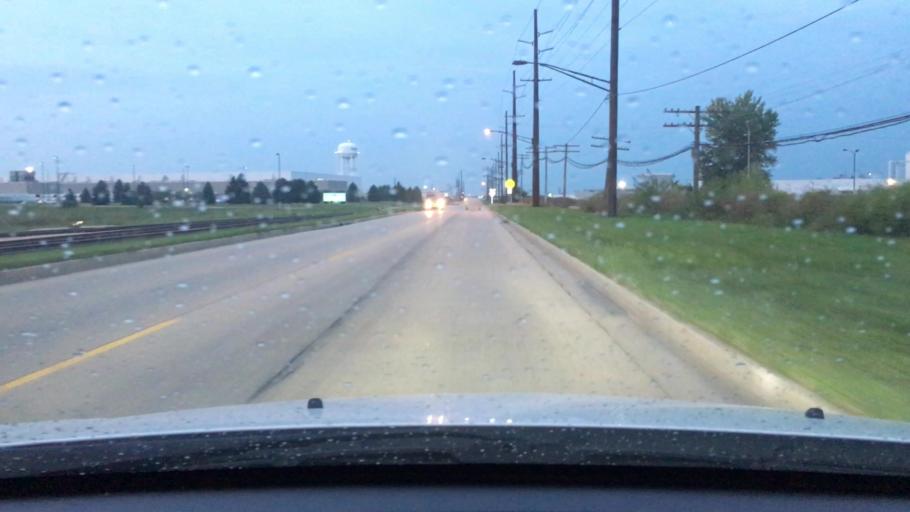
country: US
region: Illinois
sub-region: Ogle County
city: Rochelle
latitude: 41.9146
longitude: -89.0500
